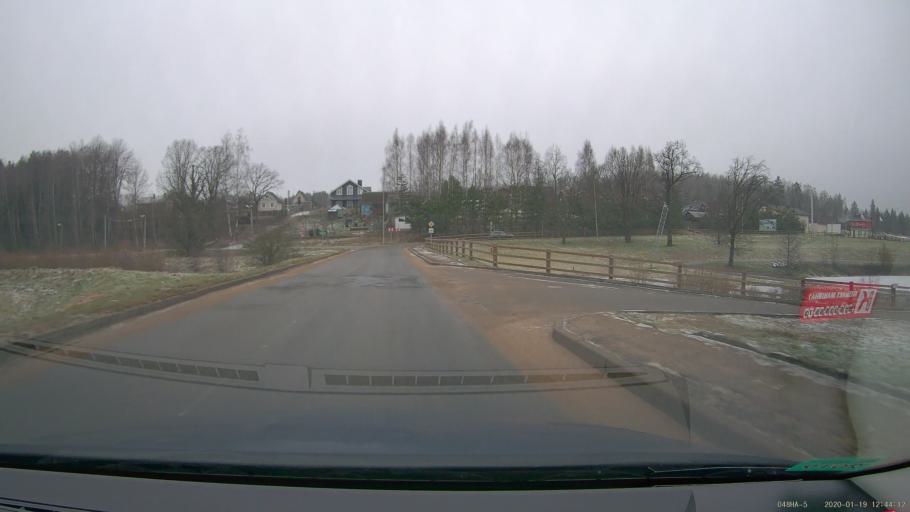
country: BY
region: Minsk
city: Lahoysk
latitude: 54.1799
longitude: 27.8073
